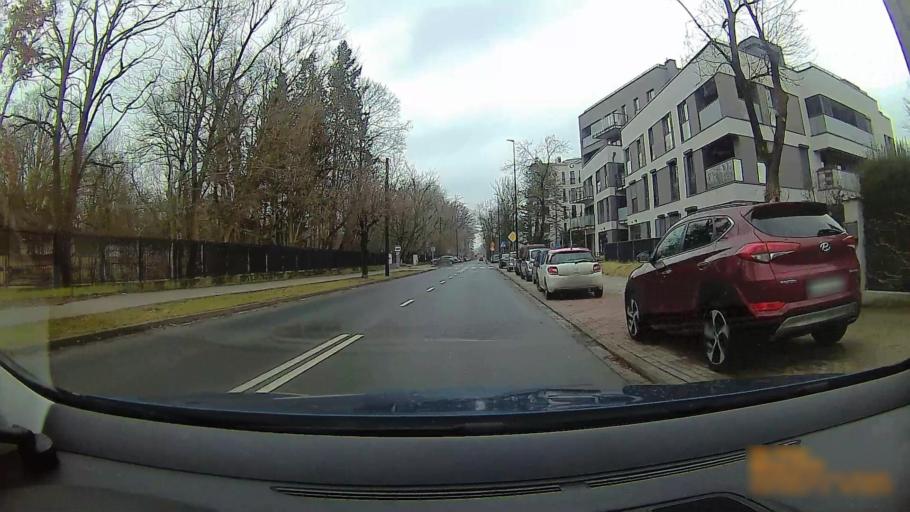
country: PL
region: Greater Poland Voivodeship
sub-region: Konin
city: Konin
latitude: 52.2091
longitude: 18.2465
